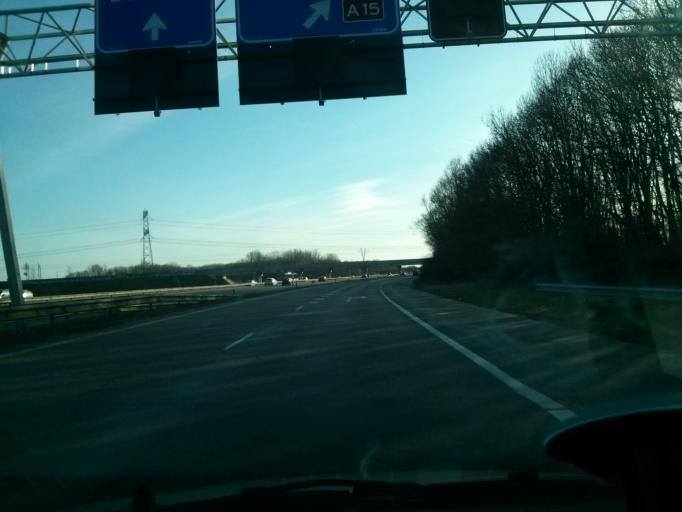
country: NL
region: Gelderland
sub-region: Gemeente Overbetuwe
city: Elst
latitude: 51.9032
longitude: 5.8716
